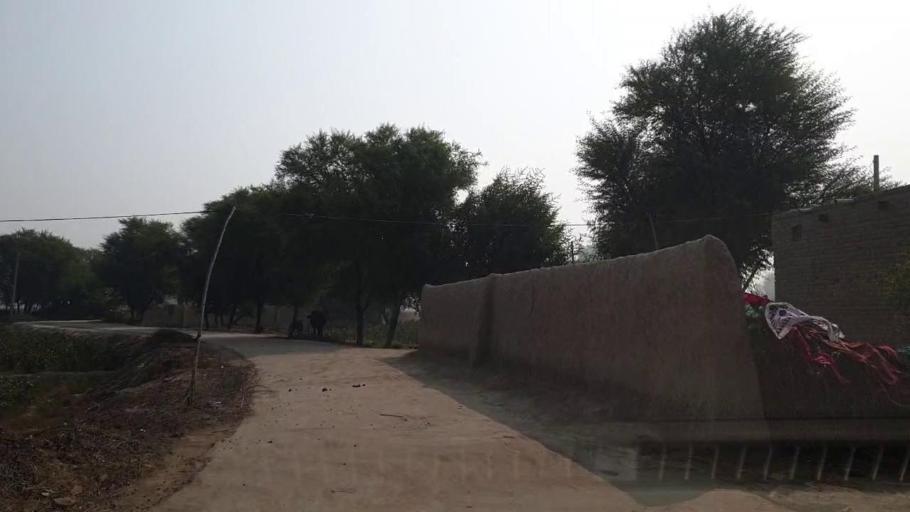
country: PK
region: Sindh
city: Sehwan
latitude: 26.4617
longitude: 67.7671
